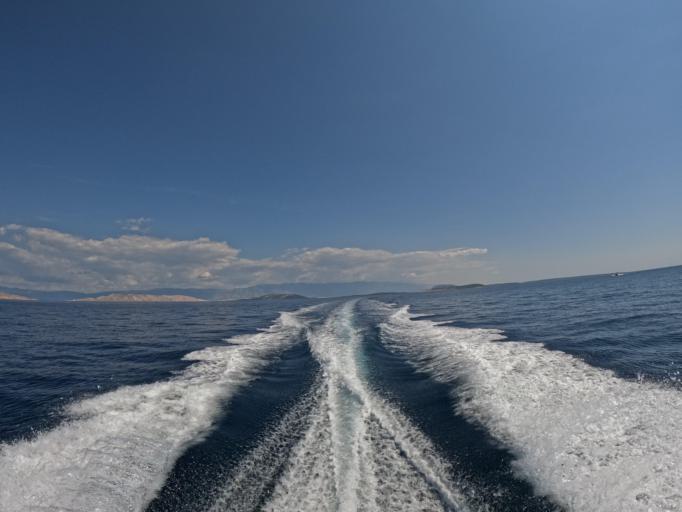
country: HR
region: Primorsko-Goranska
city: Lopar
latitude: 44.8929
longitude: 14.6286
